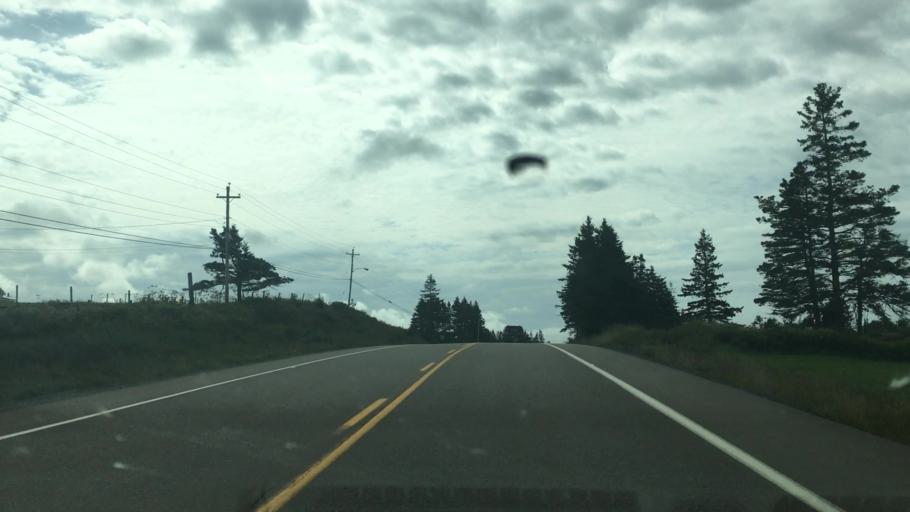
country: CA
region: Nova Scotia
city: Princeville
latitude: 45.6979
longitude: -60.7364
